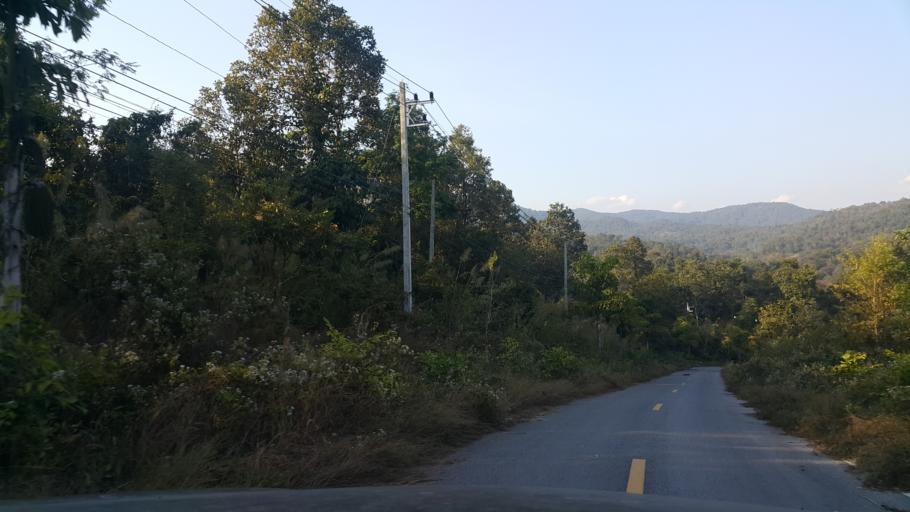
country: TH
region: Lampang
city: Hang Chat
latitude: 18.3562
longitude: 99.2462
